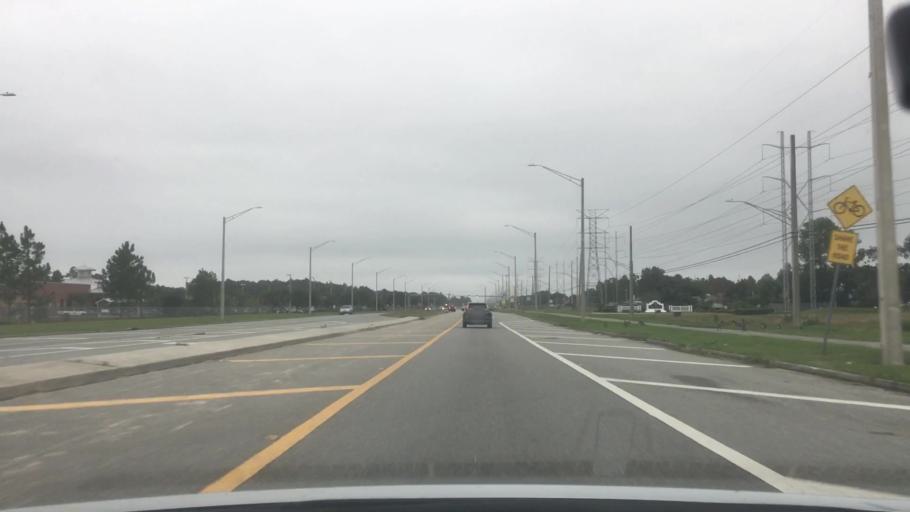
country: US
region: Florida
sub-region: Duval County
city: Atlantic Beach
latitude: 30.3310
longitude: -81.4895
